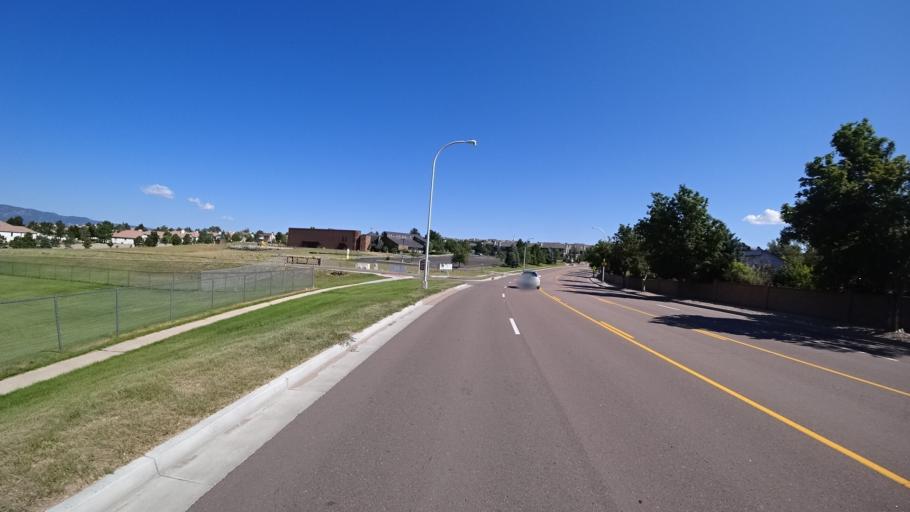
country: US
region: Colorado
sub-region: El Paso County
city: Black Forest
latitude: 38.9527
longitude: -104.7716
